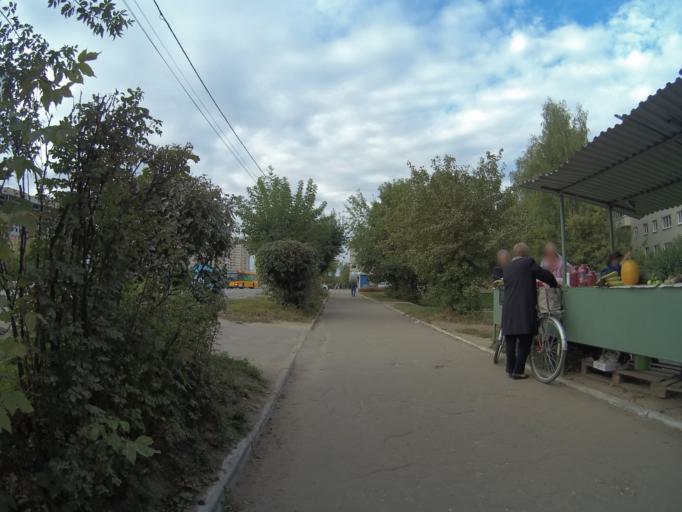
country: RU
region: Vladimir
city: Raduzhnyy
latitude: 56.1045
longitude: 40.2803
